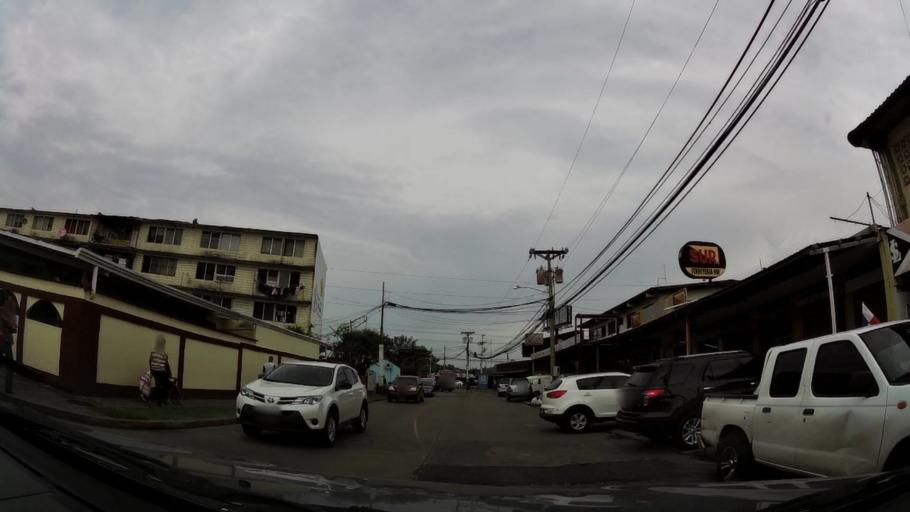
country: PA
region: Panama
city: San Miguelito
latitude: 9.0330
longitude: -79.4731
